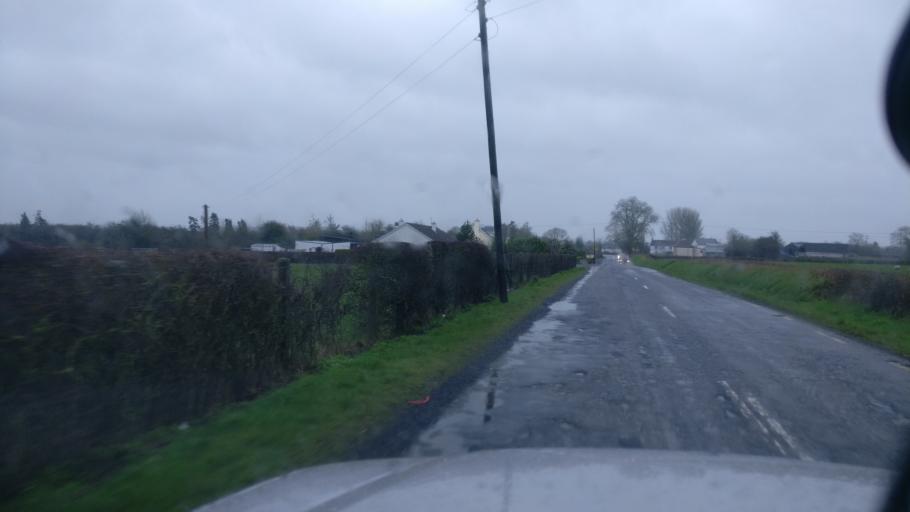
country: IE
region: Connaught
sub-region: County Galway
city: Ballinasloe
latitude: 53.2487
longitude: -8.1762
